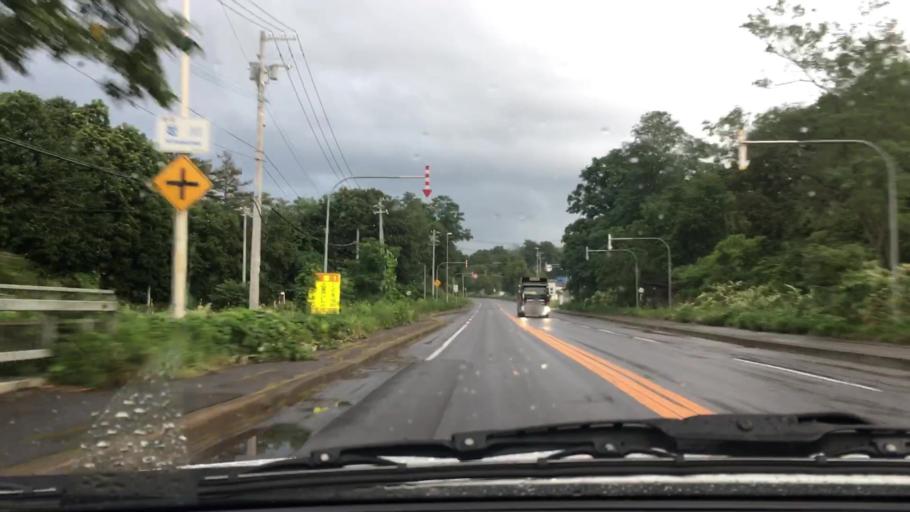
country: JP
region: Hokkaido
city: Nanae
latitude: 42.0849
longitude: 140.5850
